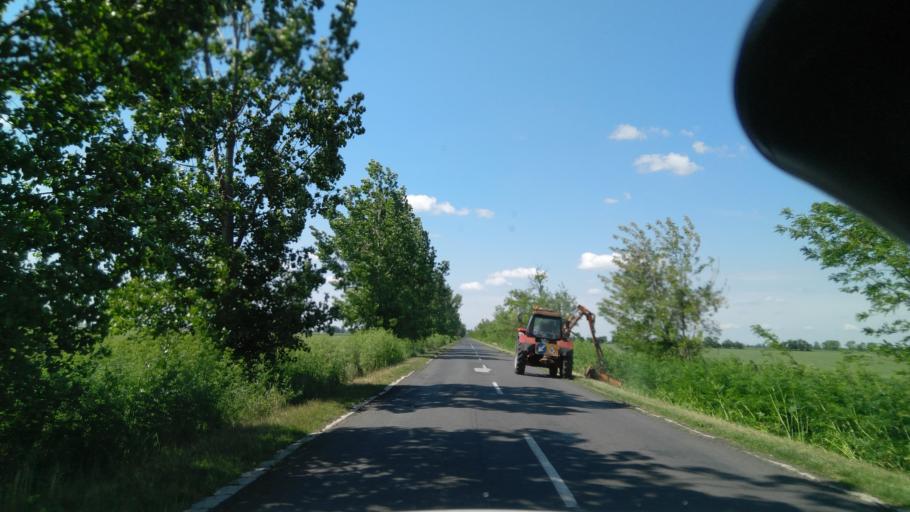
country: HU
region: Bekes
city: Medgyesegyhaza
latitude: 46.4682
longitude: 21.0134
